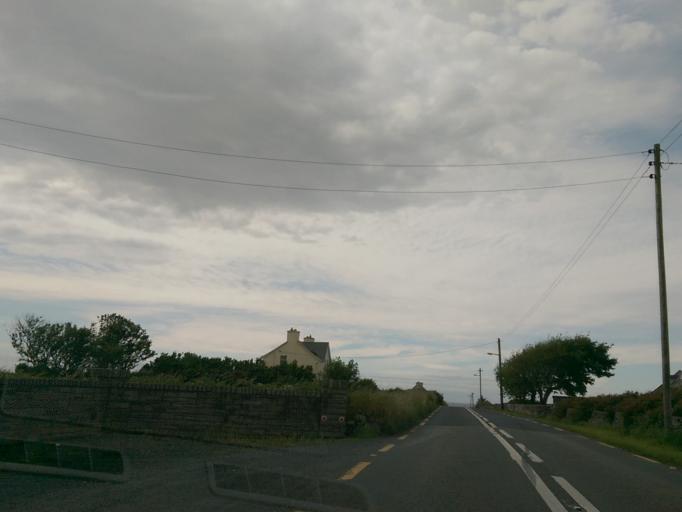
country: IE
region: Munster
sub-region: An Clar
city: Kilrush
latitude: 52.8599
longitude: -9.4062
